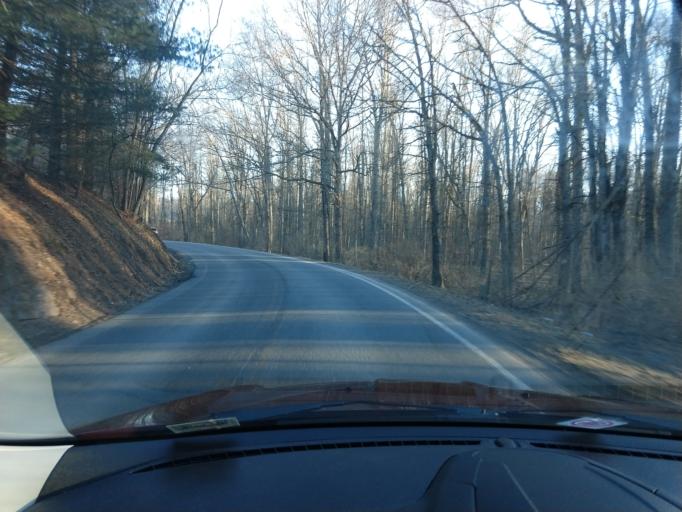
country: US
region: West Virginia
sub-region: Greenbrier County
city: Rainelle
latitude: 37.8601
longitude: -80.7185
